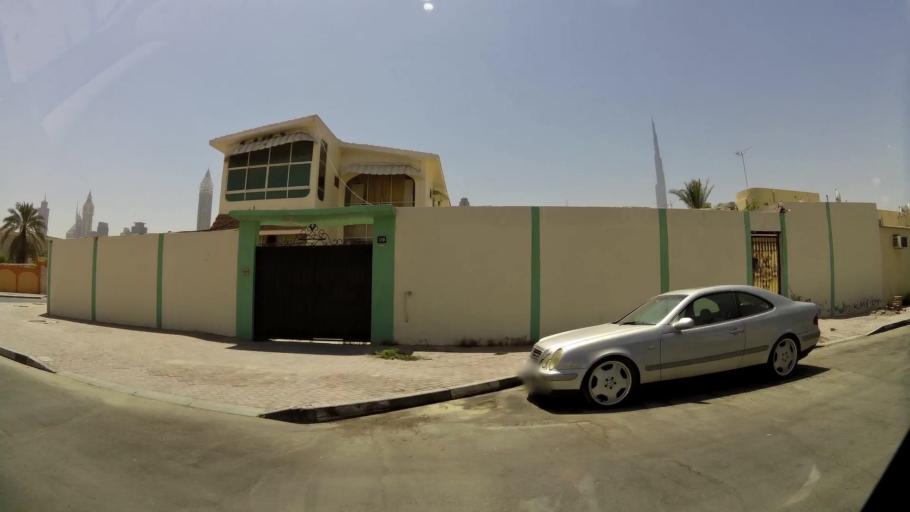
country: AE
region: Dubai
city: Dubai
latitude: 25.2126
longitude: 55.2644
